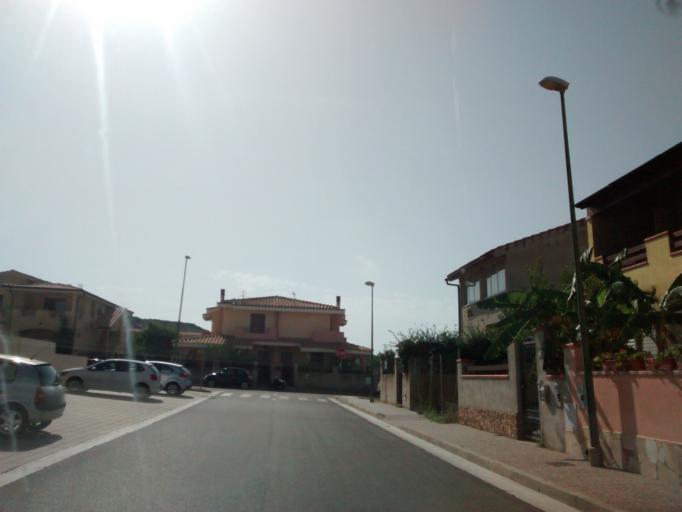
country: IT
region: Sardinia
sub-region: Provincia di Cagliari
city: Villasimius
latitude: 39.1482
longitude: 9.5189
